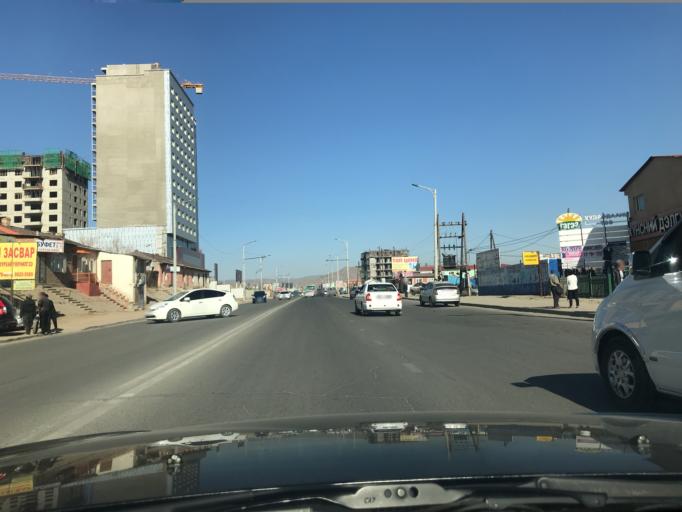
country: MN
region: Ulaanbaatar
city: Ulaanbaatar
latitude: 47.9332
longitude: 106.9061
